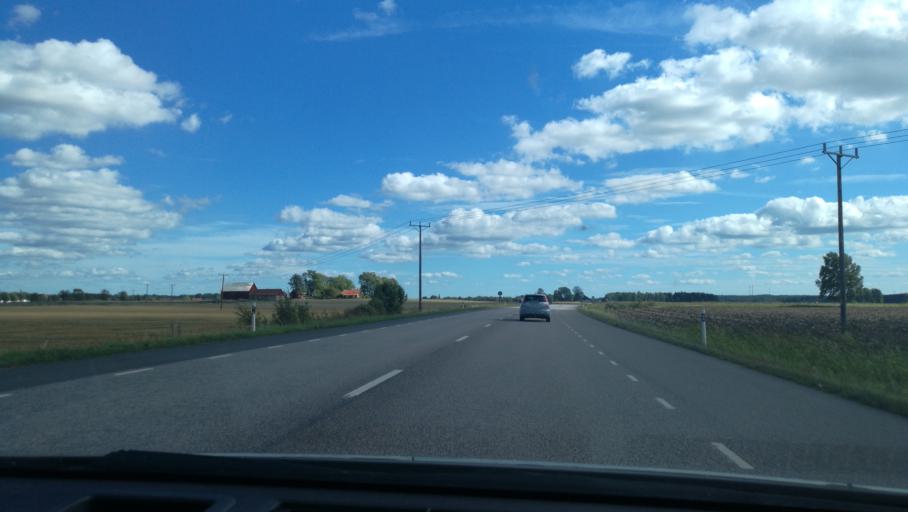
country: SE
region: Vaestra Goetaland
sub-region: Gotene Kommun
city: Kallby
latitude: 58.5108
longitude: 13.3655
